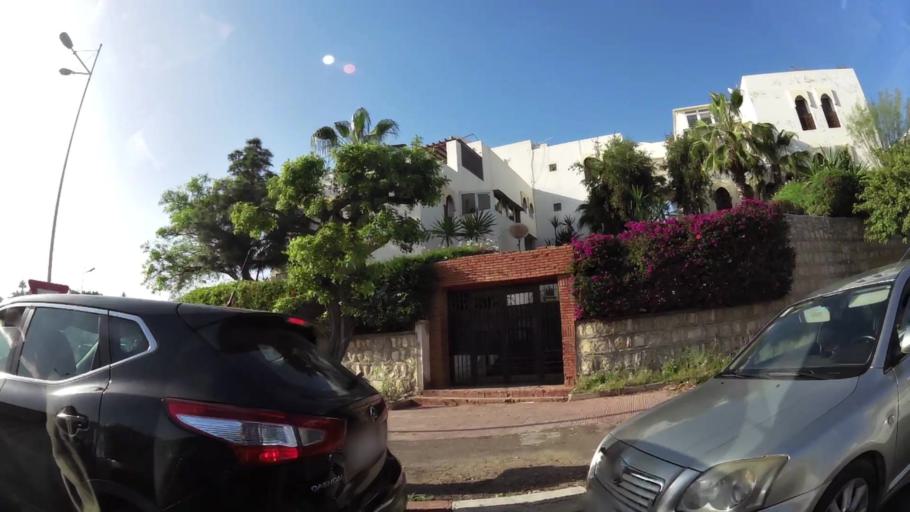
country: MA
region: Souss-Massa-Draa
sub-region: Agadir-Ida-ou-Tnan
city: Agadir
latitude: 30.4270
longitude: -9.5920
